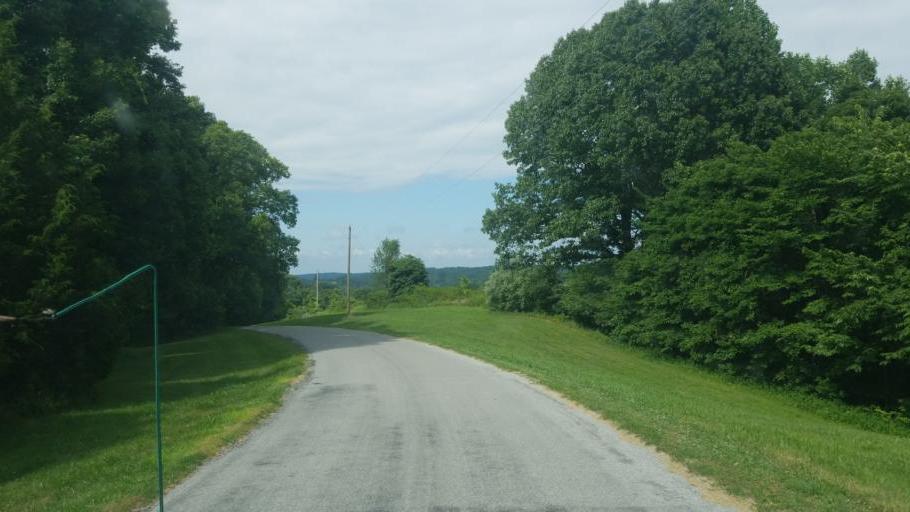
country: US
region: Illinois
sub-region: Union County
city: Cobden
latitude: 37.6121
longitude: -89.3431
